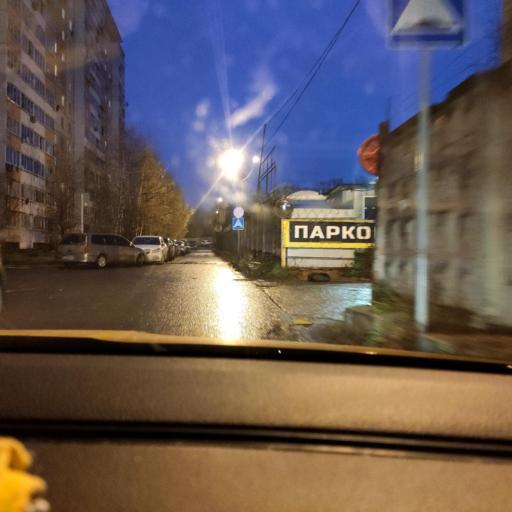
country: RU
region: Moskovskaya
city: Lesnoy Gorodok
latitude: 55.6567
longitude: 37.2038
